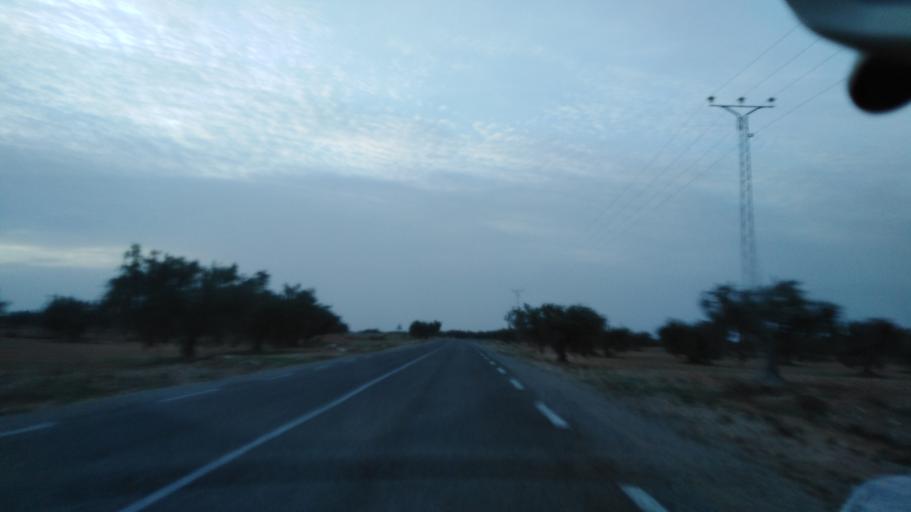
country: TN
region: Safaqis
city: Bi'r `Ali Bin Khalifah
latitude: 34.9008
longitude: 10.3901
